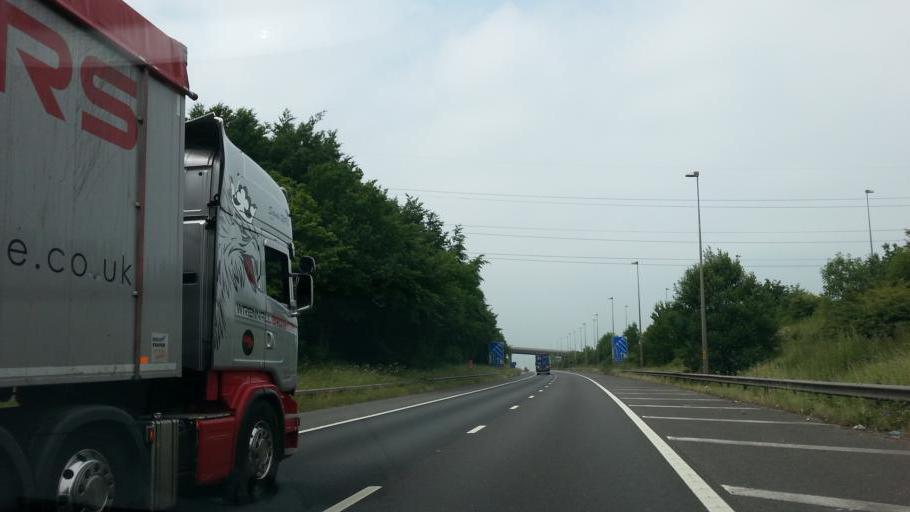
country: GB
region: England
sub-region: Staffordshire
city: Featherstone
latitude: 52.6673
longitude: -2.0713
